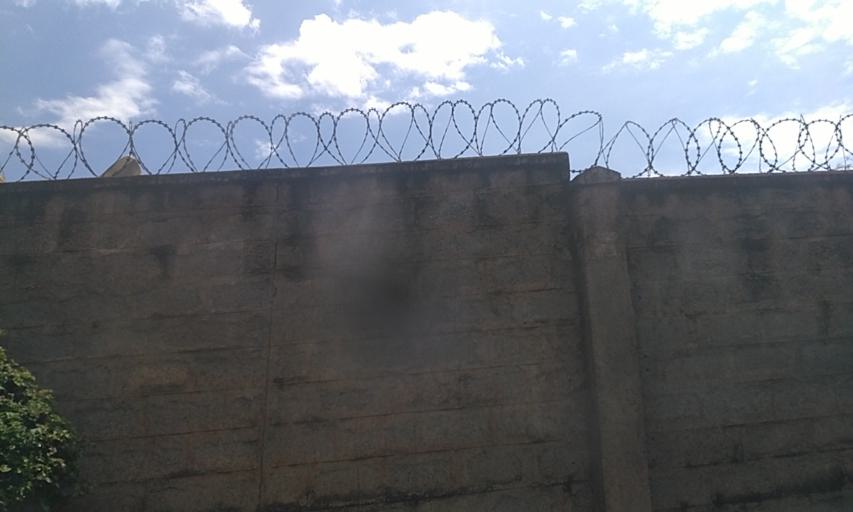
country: UG
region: Central Region
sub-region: Kampala District
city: Kampala
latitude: 0.3315
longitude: 32.5988
